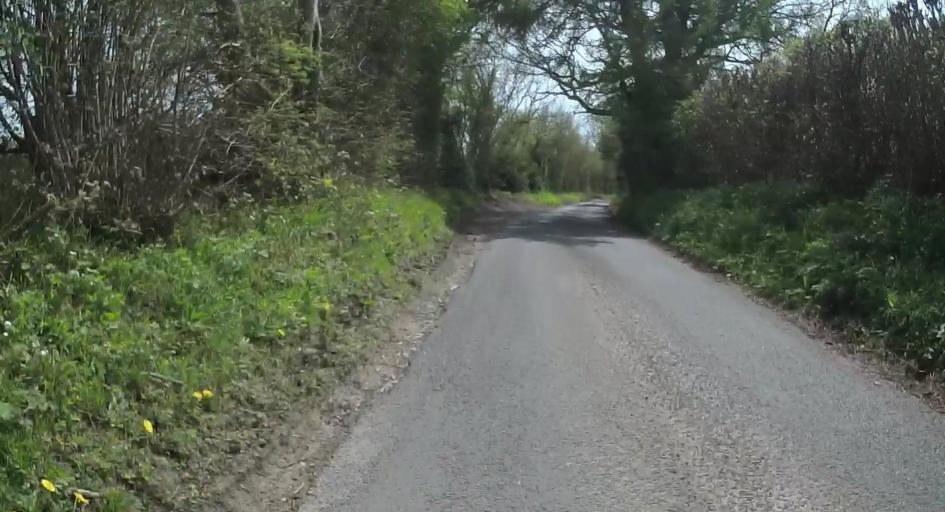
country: GB
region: England
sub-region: Hampshire
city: Alton
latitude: 51.1747
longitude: -0.9618
